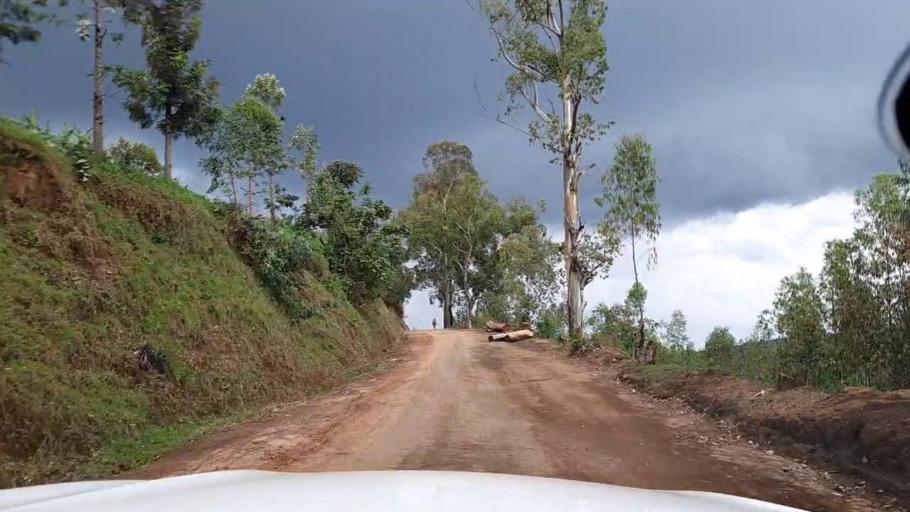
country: BI
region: Kayanza
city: Kayanza
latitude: -2.7911
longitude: 29.5237
